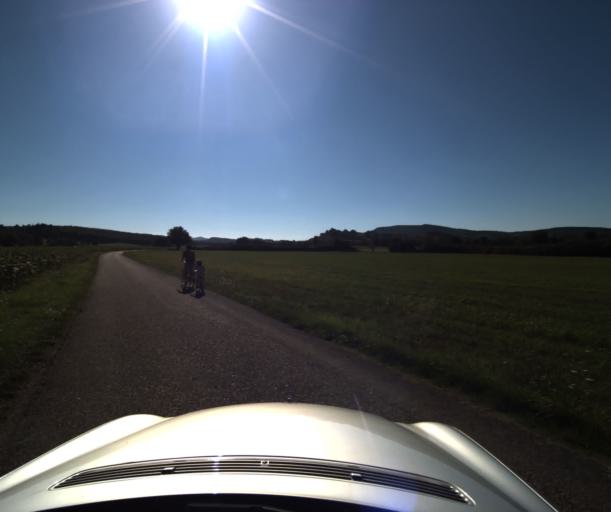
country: FR
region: Midi-Pyrenees
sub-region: Departement de l'Ariege
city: Lavelanet
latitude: 42.9841
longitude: 1.9031
